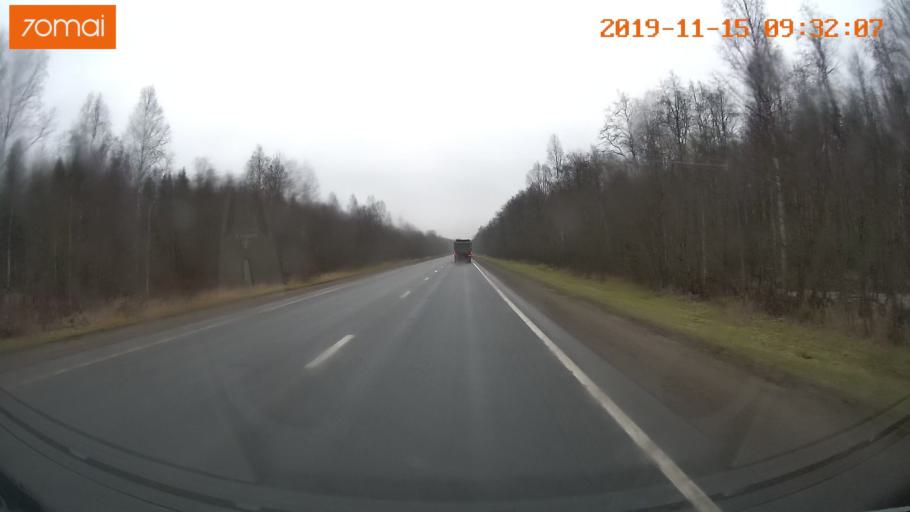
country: RU
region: Vologda
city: Sheksna
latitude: 59.2728
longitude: 38.3272
